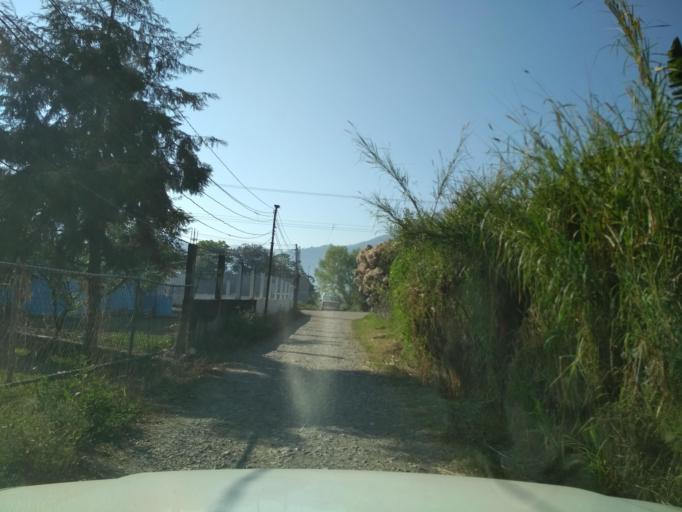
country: MX
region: Veracruz
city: Jalapilla
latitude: 18.8260
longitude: -97.0779
